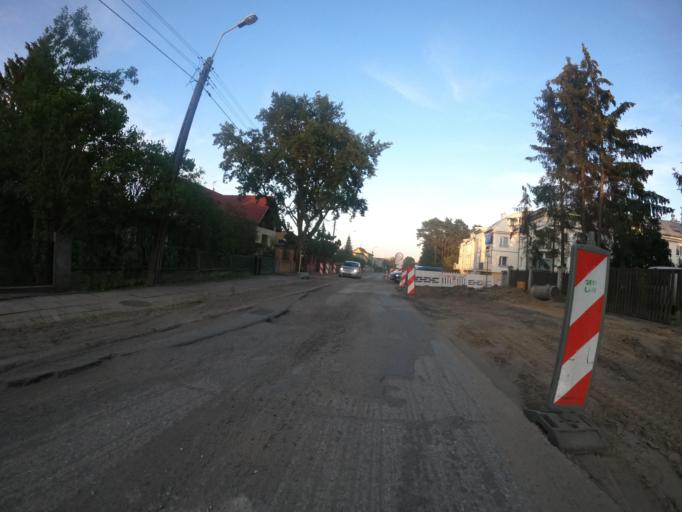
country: PL
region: West Pomeranian Voivodeship
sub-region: Powiat policki
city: Przeclaw
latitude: 53.4562
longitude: 14.4655
